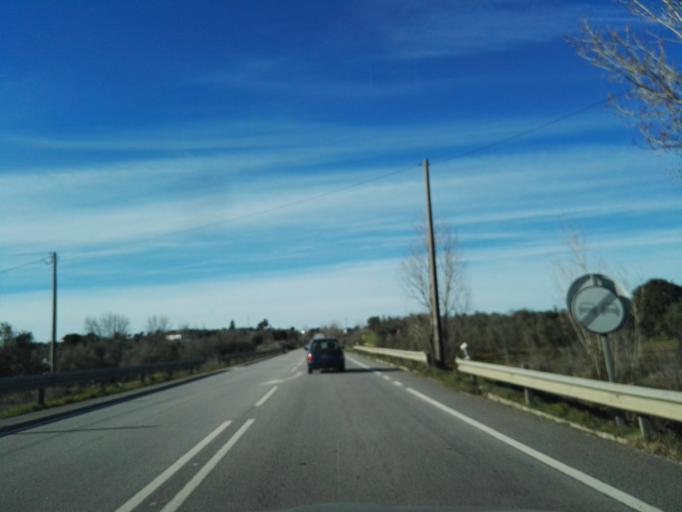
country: PT
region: Santarem
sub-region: Abrantes
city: Alferrarede
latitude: 39.4775
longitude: -8.0842
